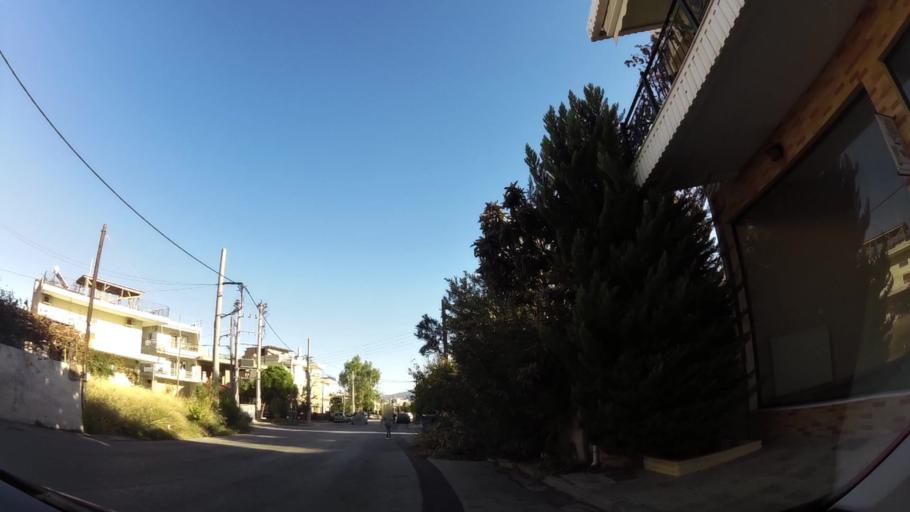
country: GR
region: Attica
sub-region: Nomarchia Anatolikis Attikis
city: Acharnes
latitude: 38.0863
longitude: 23.7236
